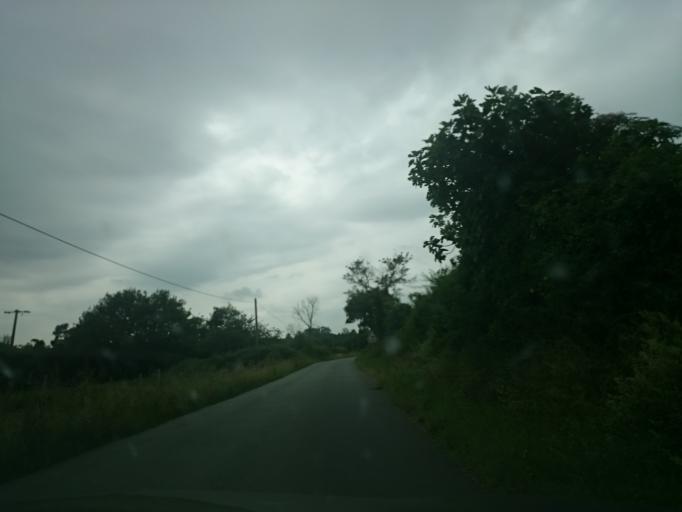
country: FR
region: Pays de la Loire
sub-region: Departement de la Loire-Atlantique
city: Le Pellerin
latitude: 47.2020
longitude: -1.7800
